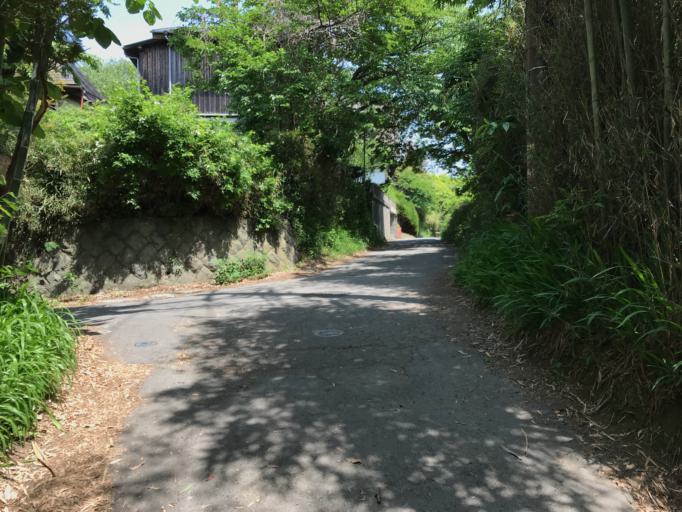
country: JP
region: Kanagawa
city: Kamakura
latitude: 35.3266
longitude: 139.5399
